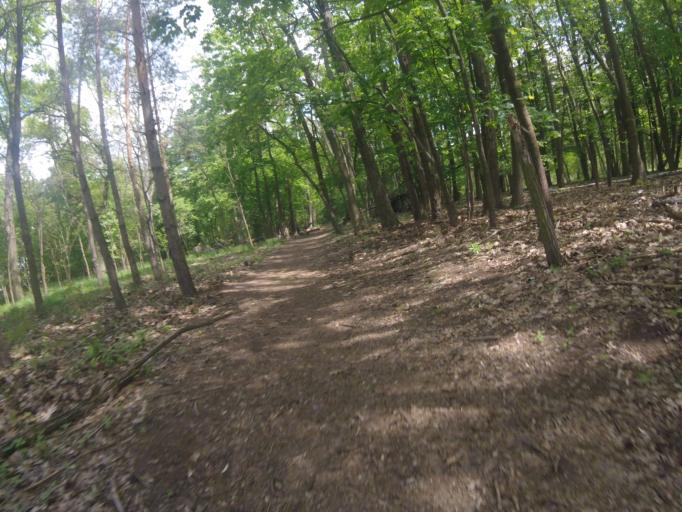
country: DE
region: Brandenburg
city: Konigs Wusterhausen
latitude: 52.2812
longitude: 13.6122
